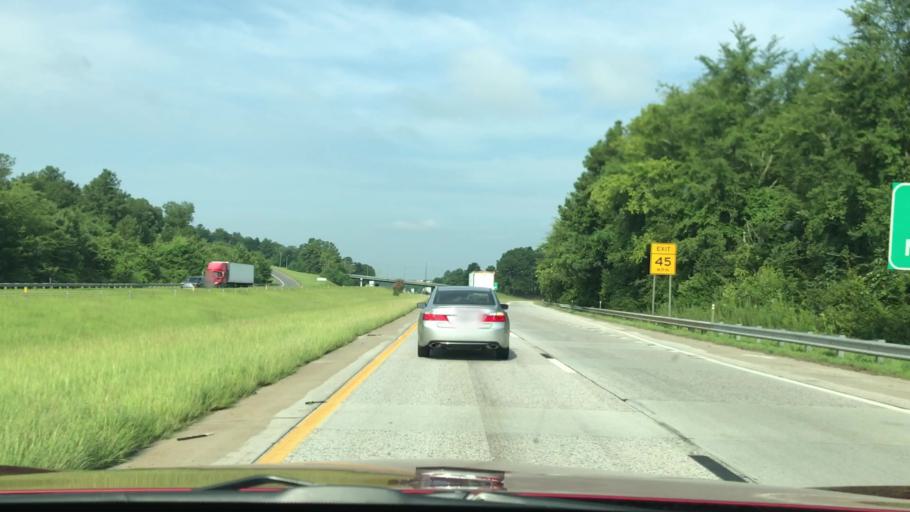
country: US
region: South Carolina
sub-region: Aiken County
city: Belvedere
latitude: 33.5419
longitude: -81.9861
